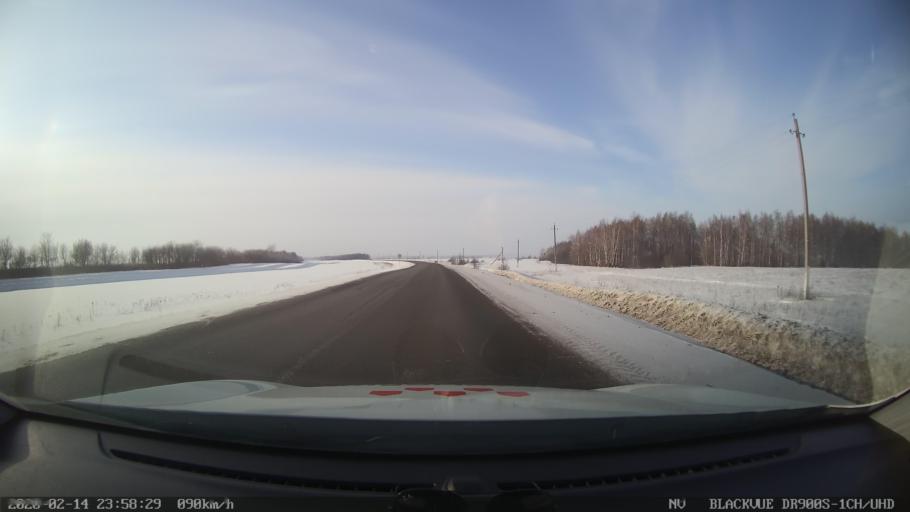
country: RU
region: Tatarstan
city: Kuybyshevskiy Zaton
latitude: 55.3410
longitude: 49.0866
